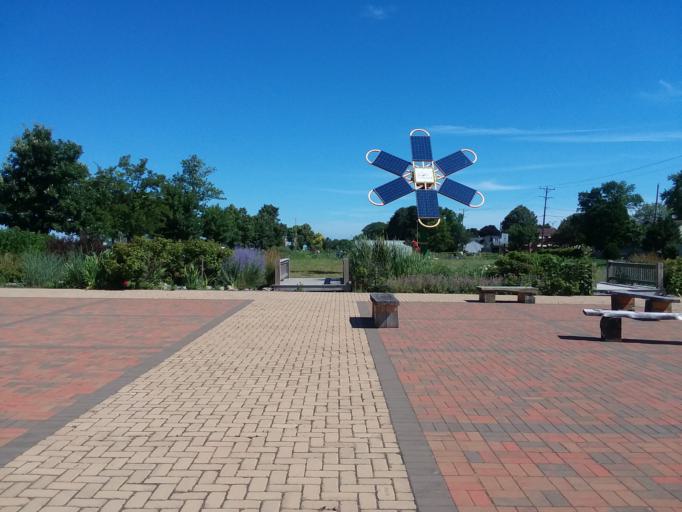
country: US
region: Wisconsin
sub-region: Milwaukee County
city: Saint Francis
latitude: 42.9723
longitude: -87.9190
